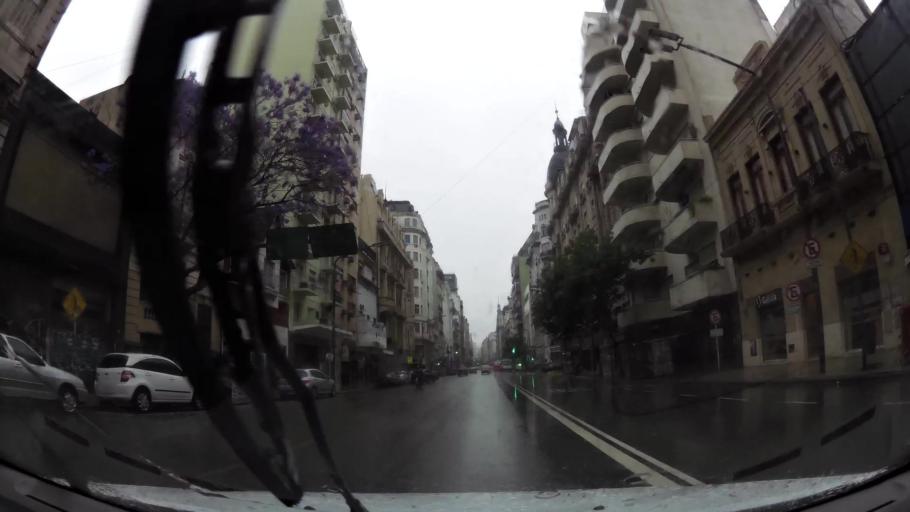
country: AR
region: Buenos Aires F.D.
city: Buenos Aires
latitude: -34.6076
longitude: -58.3921
